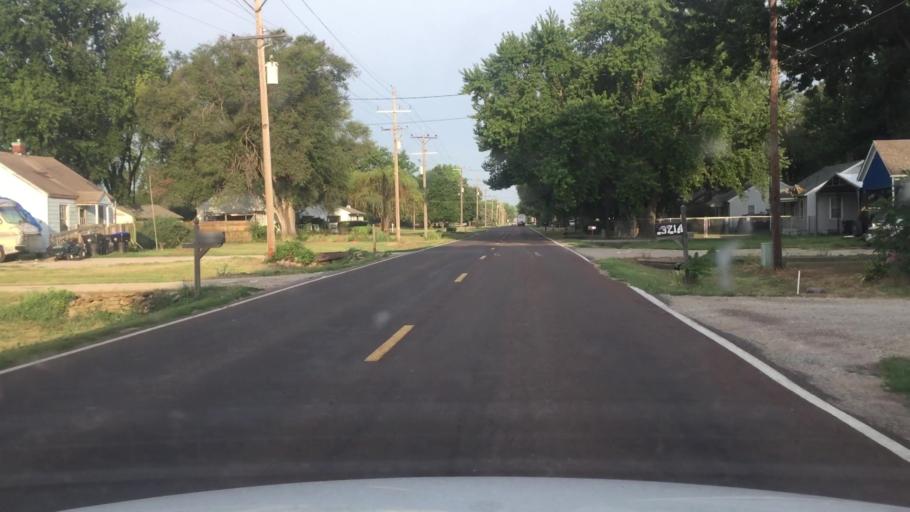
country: US
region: Kansas
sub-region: Shawnee County
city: Topeka
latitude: 39.0589
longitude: -95.6159
